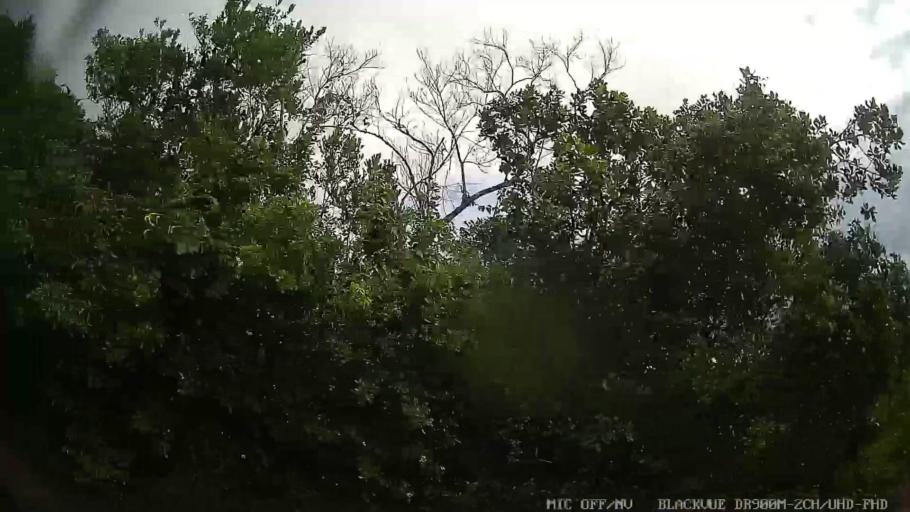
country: BR
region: Sao Paulo
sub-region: Peruibe
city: Peruibe
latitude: -24.2460
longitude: -46.8991
